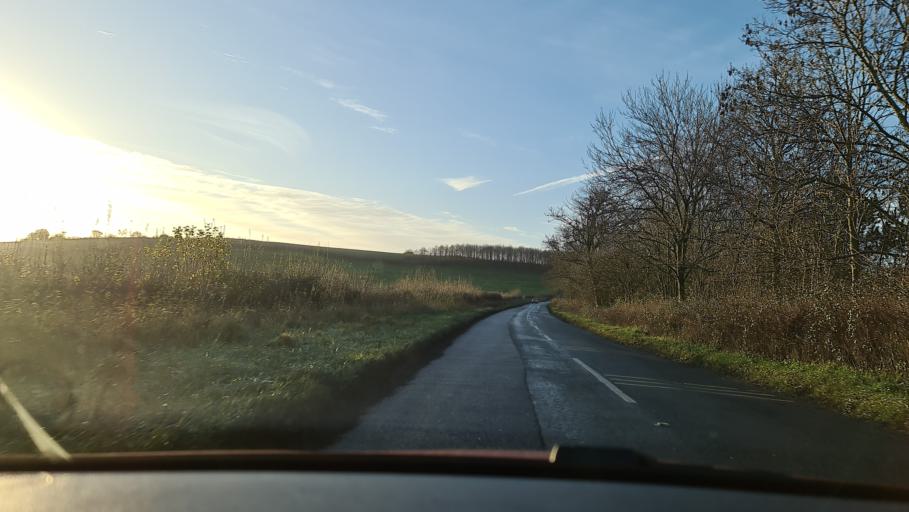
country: GB
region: England
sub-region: Buckinghamshire
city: Waddesdon
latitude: 51.8396
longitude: -0.9030
